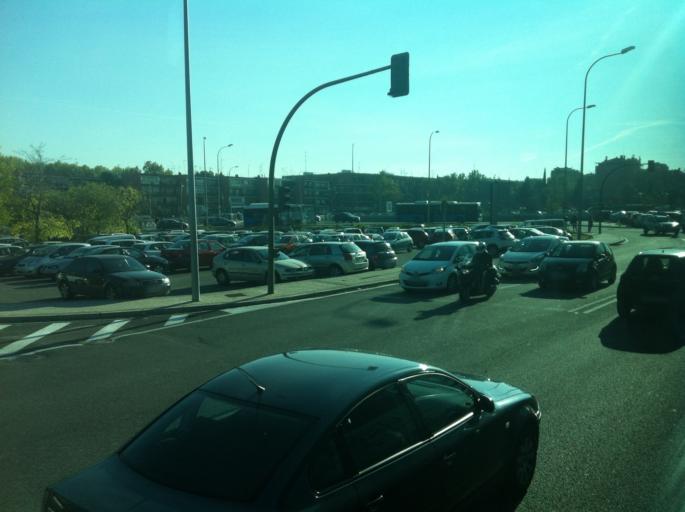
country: ES
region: Madrid
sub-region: Provincia de Madrid
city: San Blas
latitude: 40.4508
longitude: -3.6081
